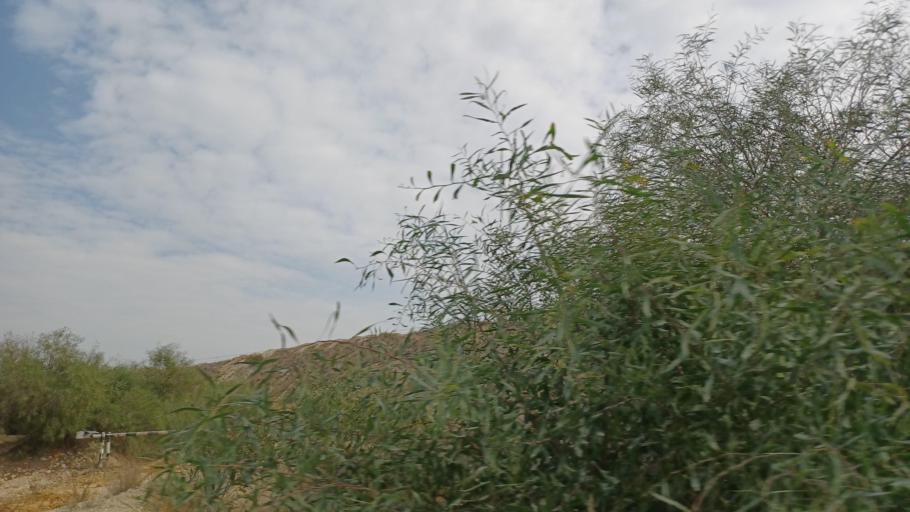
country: CY
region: Lefkosia
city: Meniko
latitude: 35.0632
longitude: 33.1276
